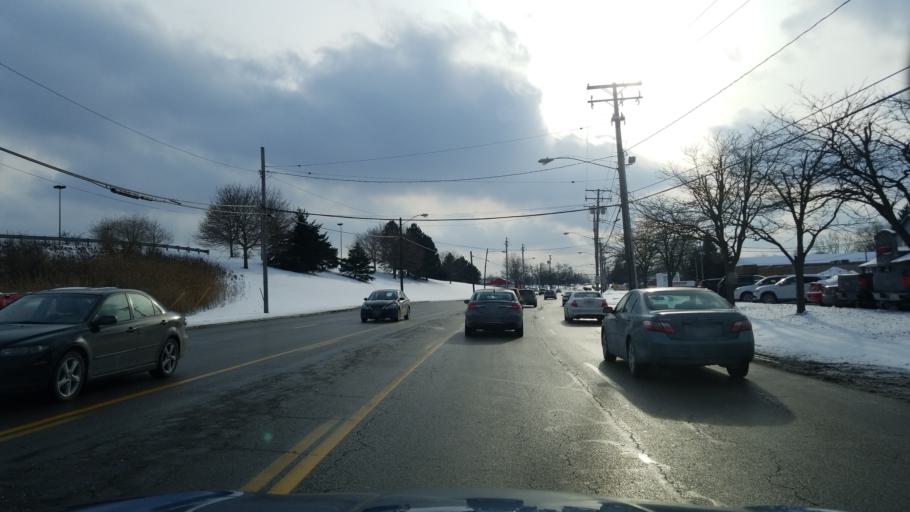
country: US
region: Ohio
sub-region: Cuyahoga County
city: Middleburg Heights
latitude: 41.3497
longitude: -81.8213
